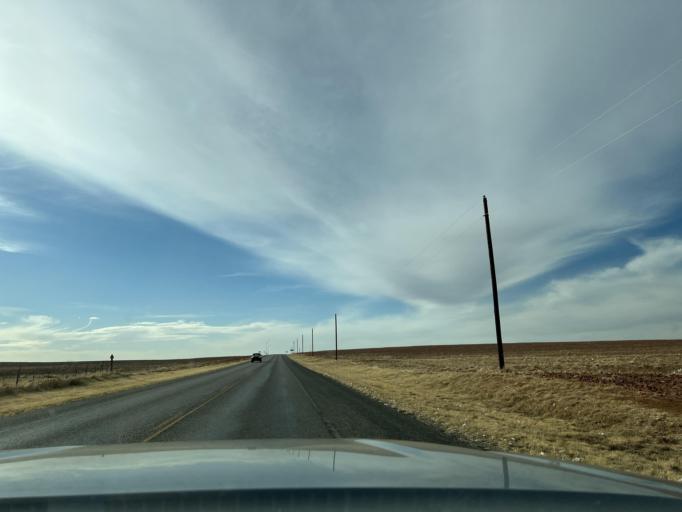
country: US
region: Texas
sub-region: Fisher County
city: Roby
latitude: 32.7407
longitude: -100.4857
